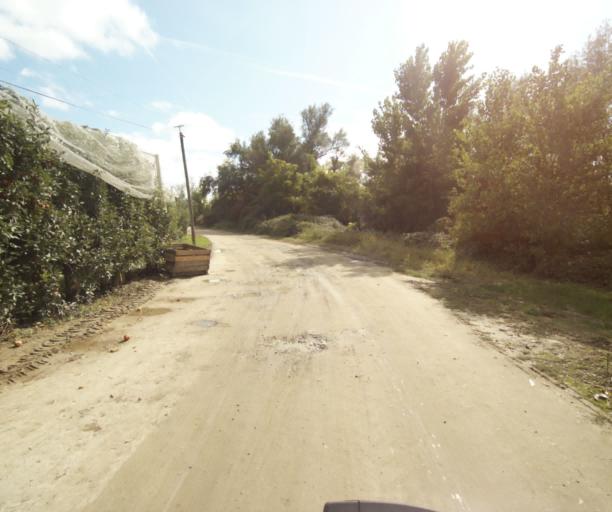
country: FR
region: Midi-Pyrenees
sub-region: Departement du Tarn-et-Garonne
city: Montech
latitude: 43.9515
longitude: 1.1866
